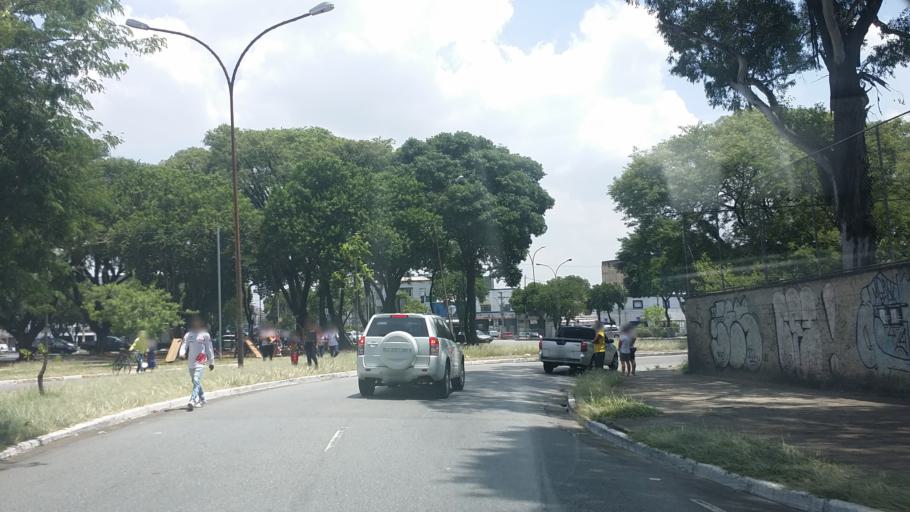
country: BR
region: Sao Paulo
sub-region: Sao Paulo
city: Sao Paulo
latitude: -23.5257
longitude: -46.6108
